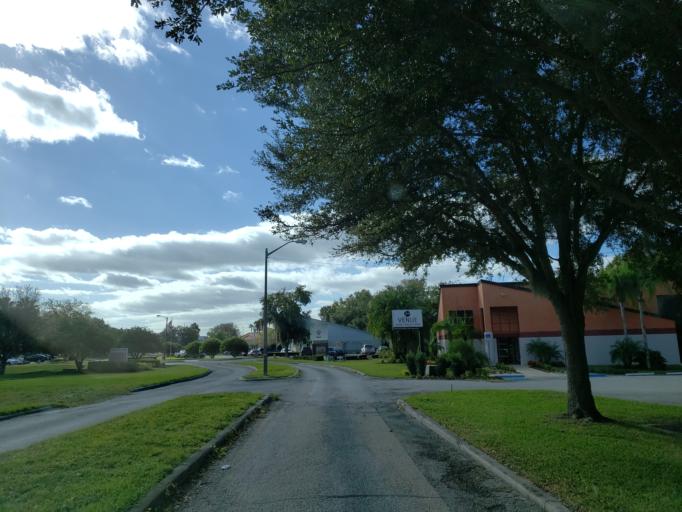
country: US
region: Florida
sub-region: Polk County
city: Medulla
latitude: 27.9742
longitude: -81.9638
